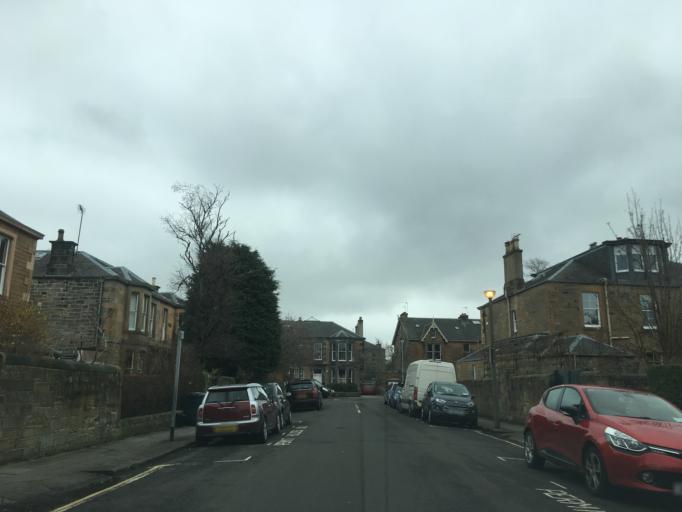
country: GB
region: Scotland
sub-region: Edinburgh
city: Edinburgh
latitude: 55.9375
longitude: -3.1872
